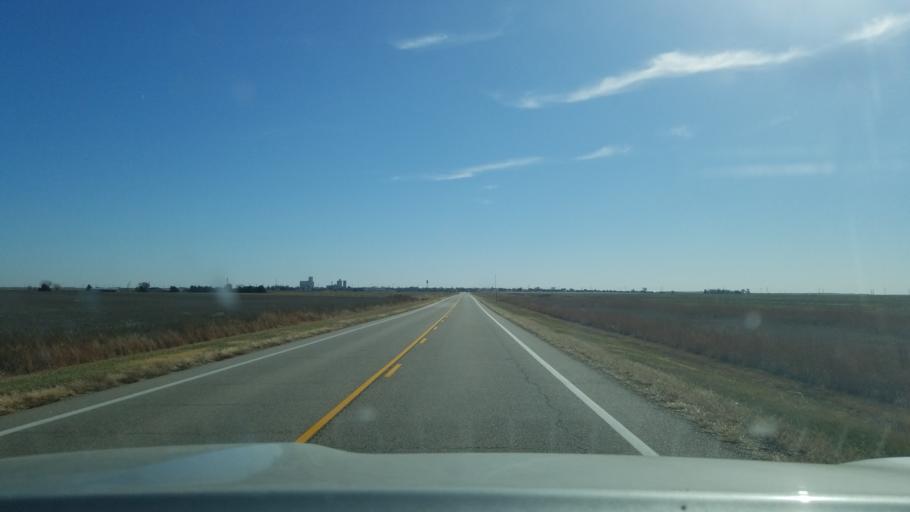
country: US
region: Kansas
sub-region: Kiowa County
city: Greensburg
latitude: 37.5654
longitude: -99.6566
